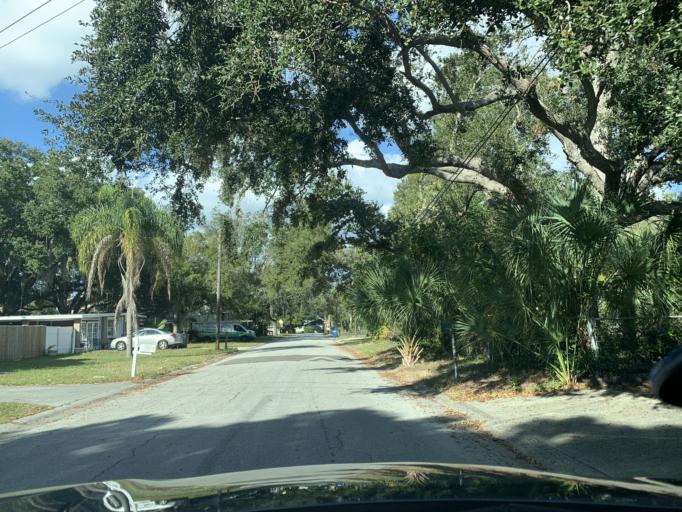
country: US
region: Florida
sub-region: Pinellas County
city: Belleair
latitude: 27.9414
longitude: -82.7928
